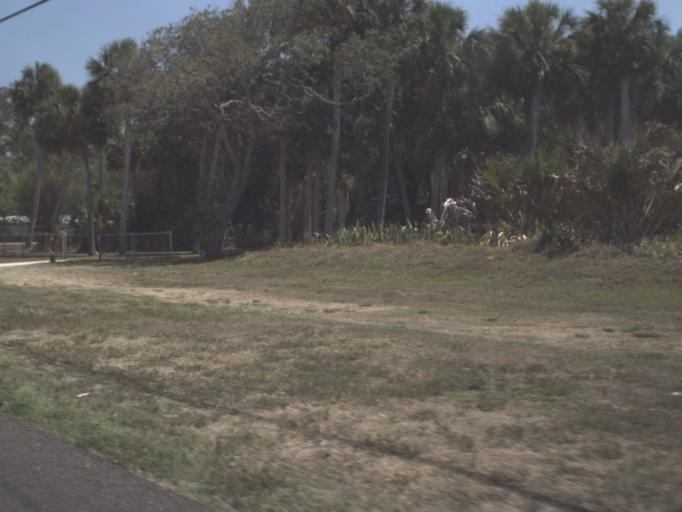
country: US
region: Florida
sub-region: Brevard County
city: Malabar
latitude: 27.9996
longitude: -80.5605
